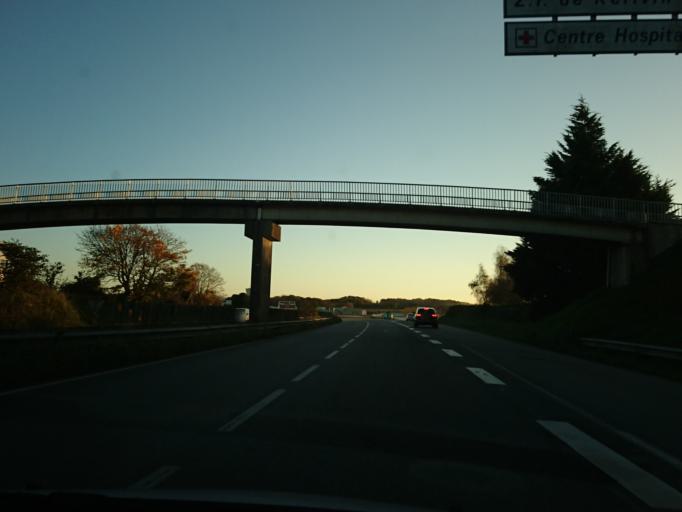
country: FR
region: Brittany
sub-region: Departement du Finistere
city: Morlaix
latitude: 48.5785
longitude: -3.8536
